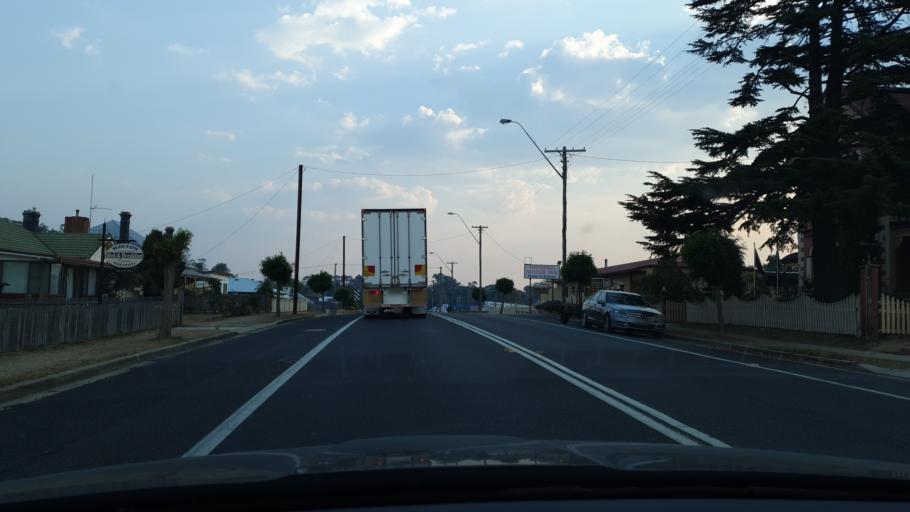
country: AU
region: New South Wales
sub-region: Tenterfield Municipality
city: Carrolls Creek
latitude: -29.0601
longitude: 152.0179
